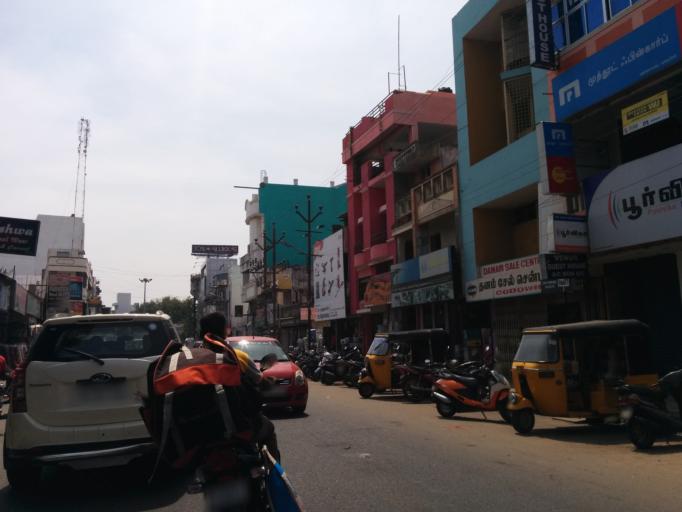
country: IN
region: Pondicherry
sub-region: Puducherry
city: Puducherry
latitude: 11.9381
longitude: 79.8257
